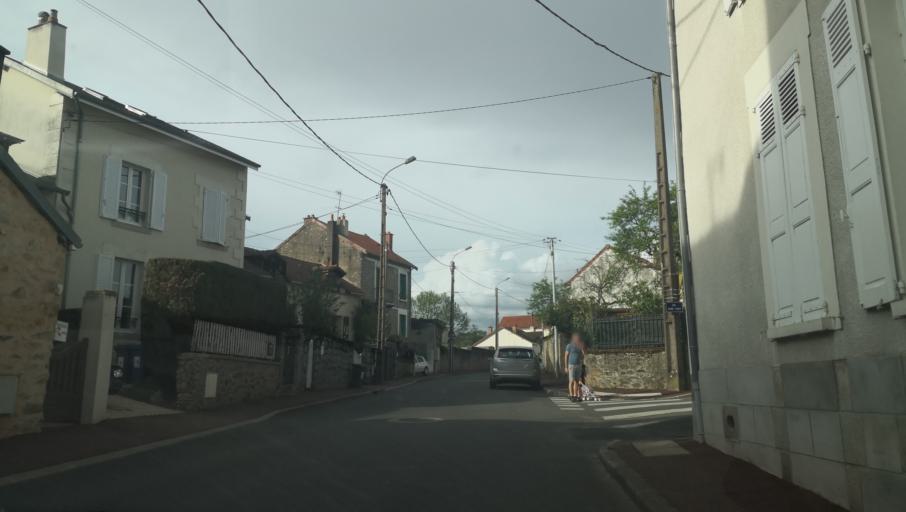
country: FR
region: Limousin
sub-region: Departement de la Haute-Vienne
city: Limoges
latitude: 45.8487
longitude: 1.2495
